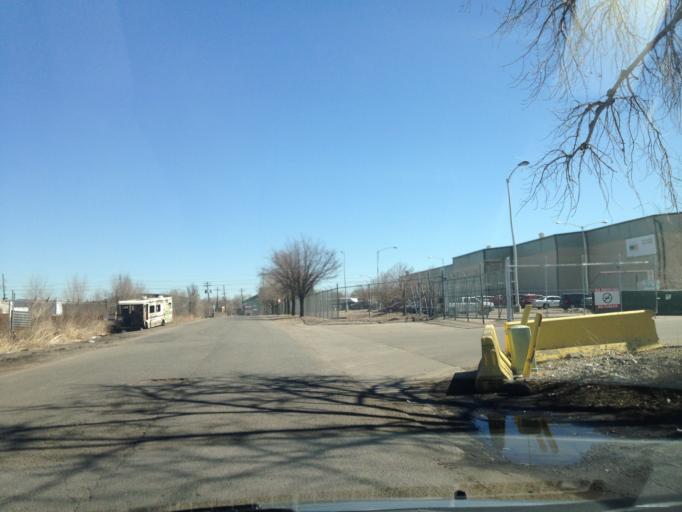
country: US
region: Colorado
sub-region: Adams County
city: Commerce City
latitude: 39.7954
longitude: -104.9715
